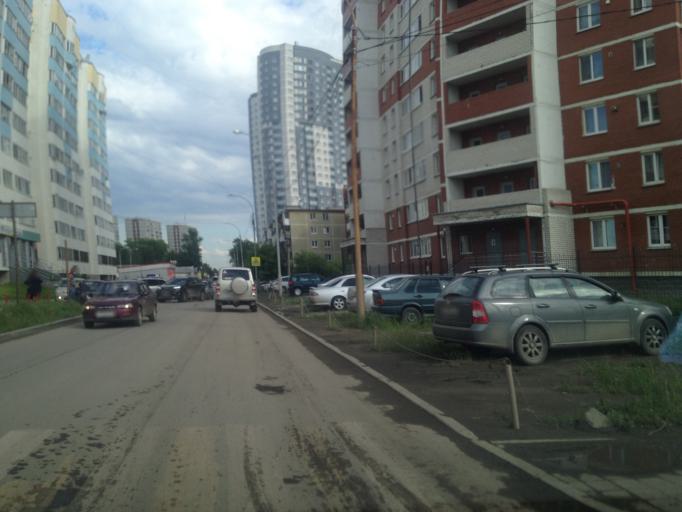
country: RU
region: Sverdlovsk
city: Yekaterinburg
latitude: 56.8735
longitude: 60.5434
